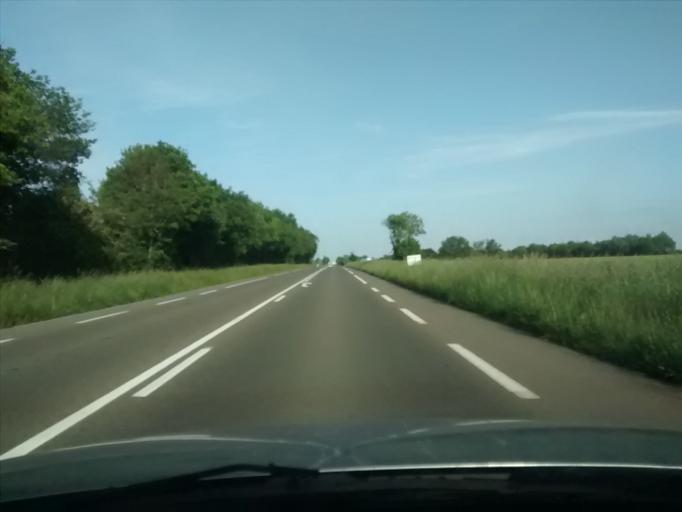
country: FR
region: Pays de la Loire
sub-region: Departement de la Mayenne
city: Soulge-sur-Ouette
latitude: 48.0503
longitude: -0.5265
